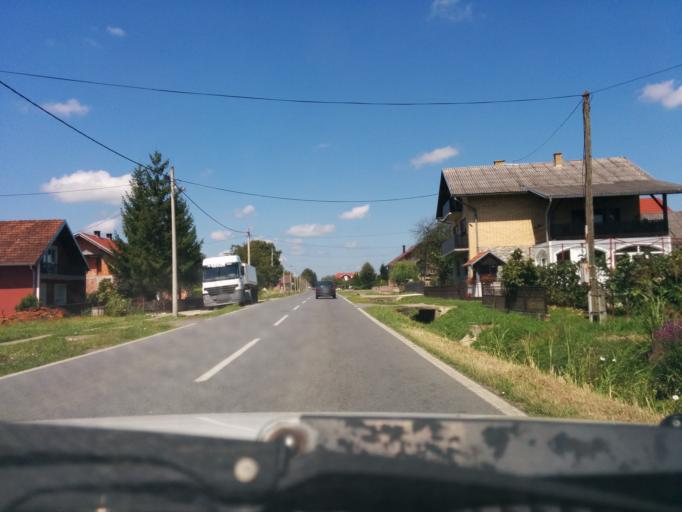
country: HR
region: Sisacko-Moslavacka
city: Lipovljani
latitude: 45.3685
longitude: 16.9293
